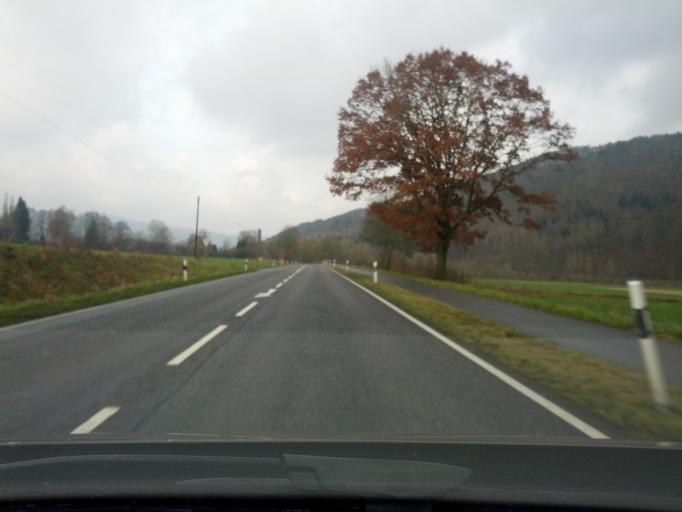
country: DE
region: Lower Saxony
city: Buhren
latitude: 51.4690
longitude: 9.6392
